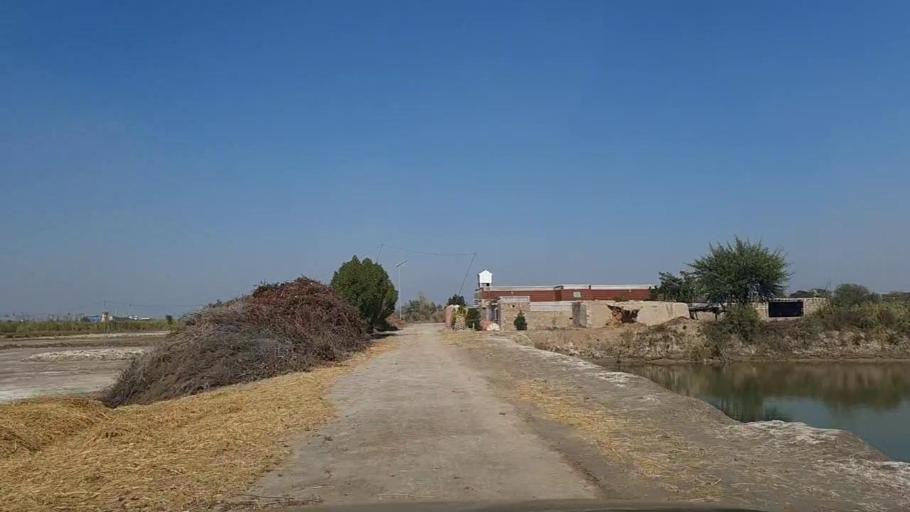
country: PK
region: Sindh
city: Bandhi
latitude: 26.5244
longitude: 68.3109
